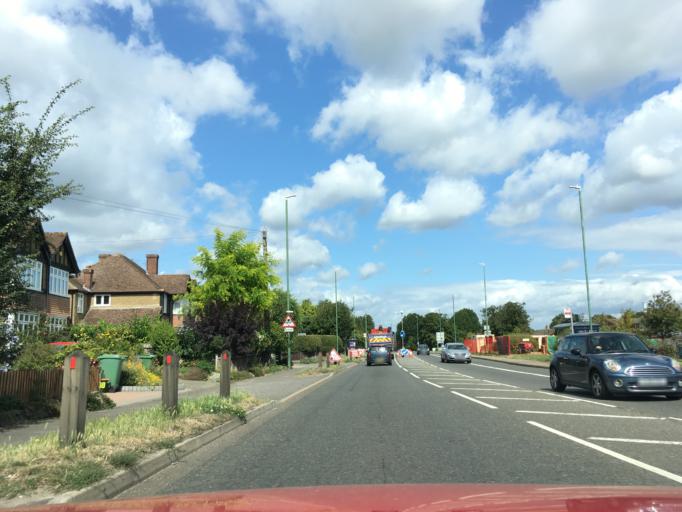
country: GB
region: England
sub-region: Kent
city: Aylesford
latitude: 51.2856
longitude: 0.4936
